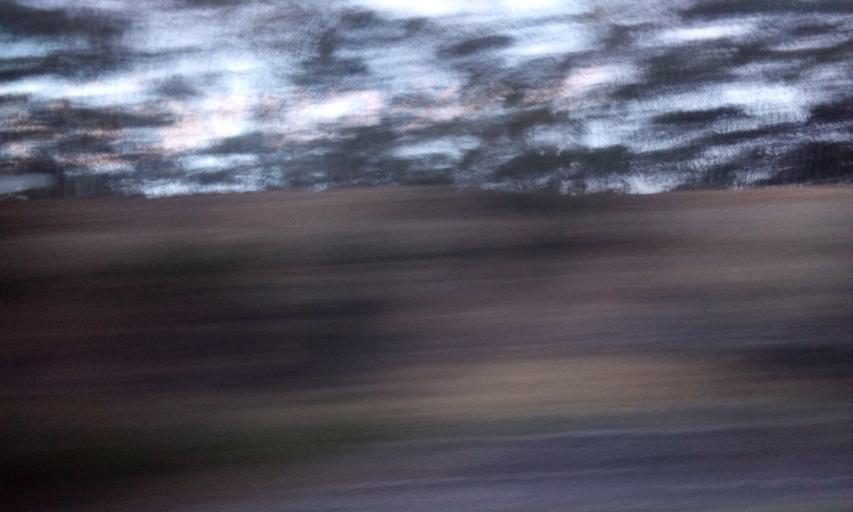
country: AU
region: New South Wales
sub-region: Wingecarribee
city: Bundanoon
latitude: -34.6501
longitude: 150.0987
